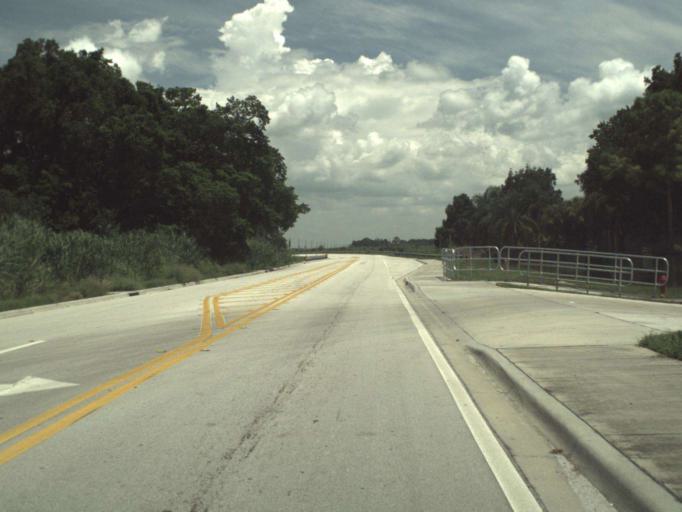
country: US
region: Florida
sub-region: Palm Beach County
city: Pahokee
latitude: 26.8616
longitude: -80.6306
